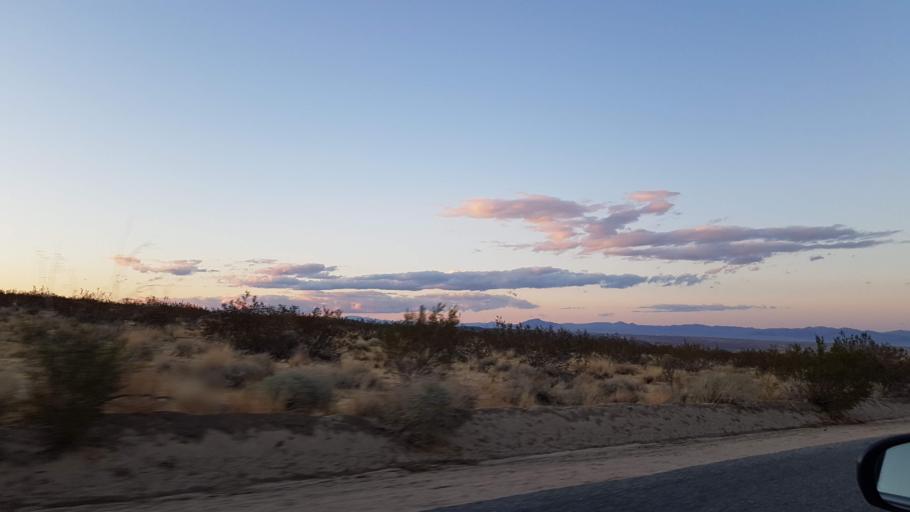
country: US
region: California
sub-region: San Bernardino County
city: Twentynine Palms
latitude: 34.1056
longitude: -116.1525
